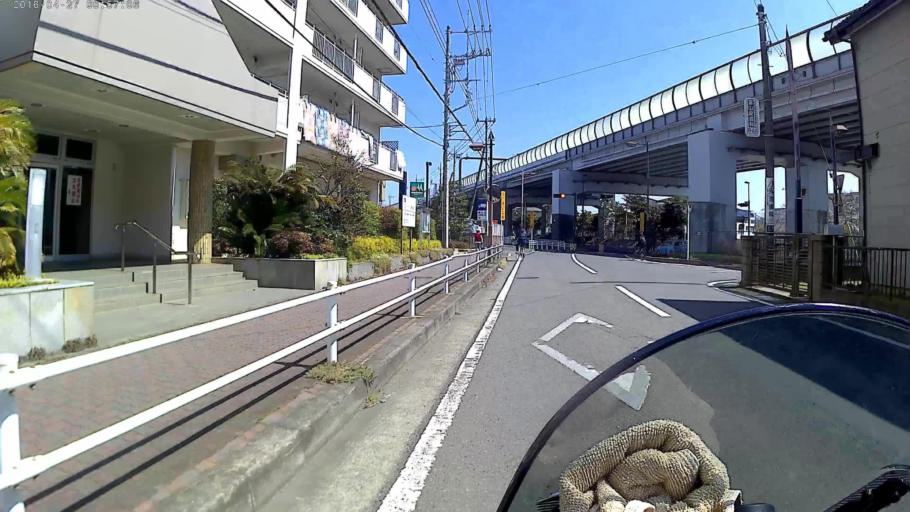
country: JP
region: Kanagawa
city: Chigasaki
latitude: 35.3504
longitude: 139.4062
